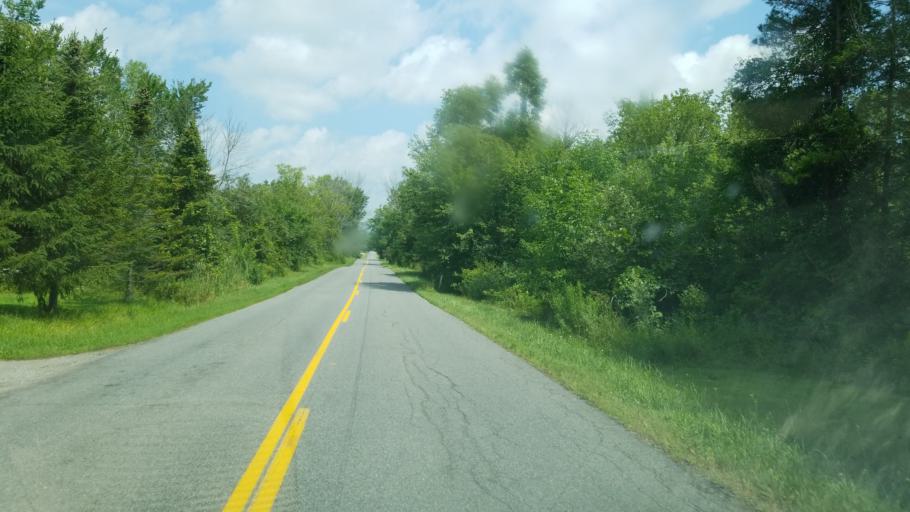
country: US
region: Michigan
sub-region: Kent County
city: Cedar Springs
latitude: 43.2551
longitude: -85.5113
